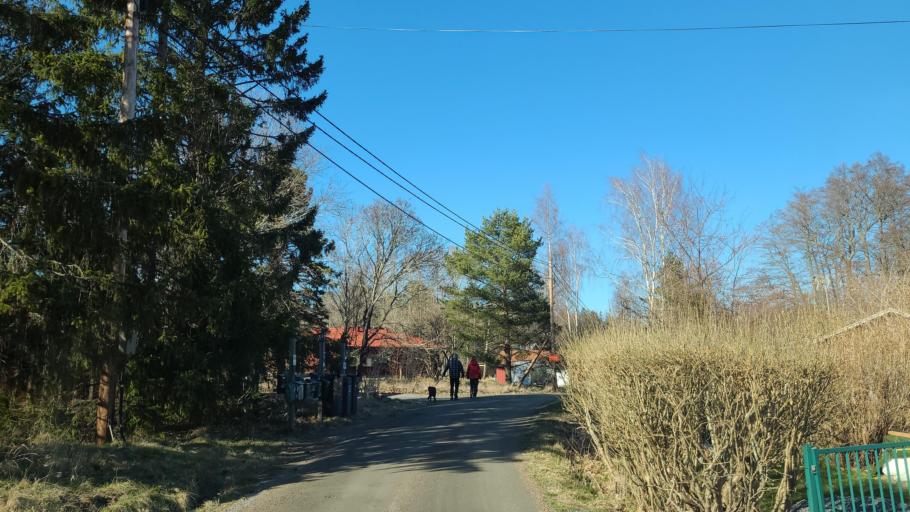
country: SE
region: Stockholm
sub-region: Varmdo Kommun
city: Holo
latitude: 59.3581
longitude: 18.6654
